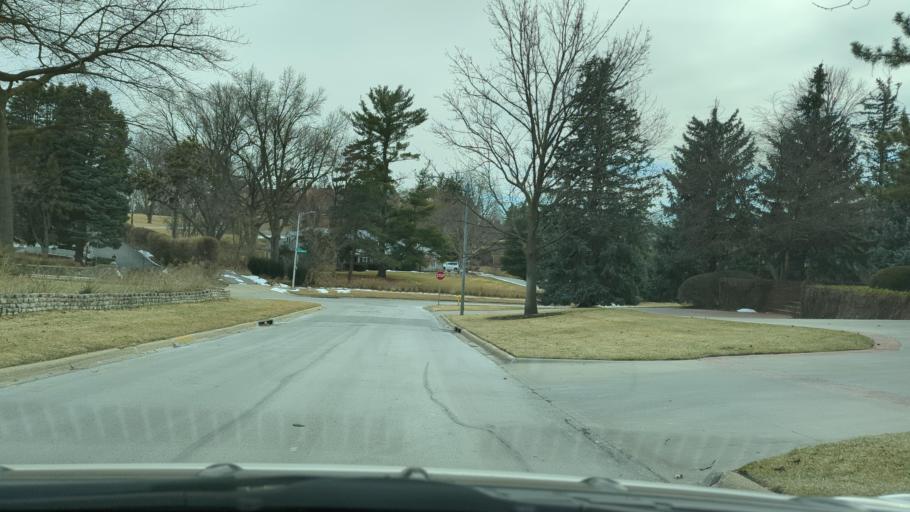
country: US
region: Nebraska
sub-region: Douglas County
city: Ralston
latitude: 41.2654
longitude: -96.0143
